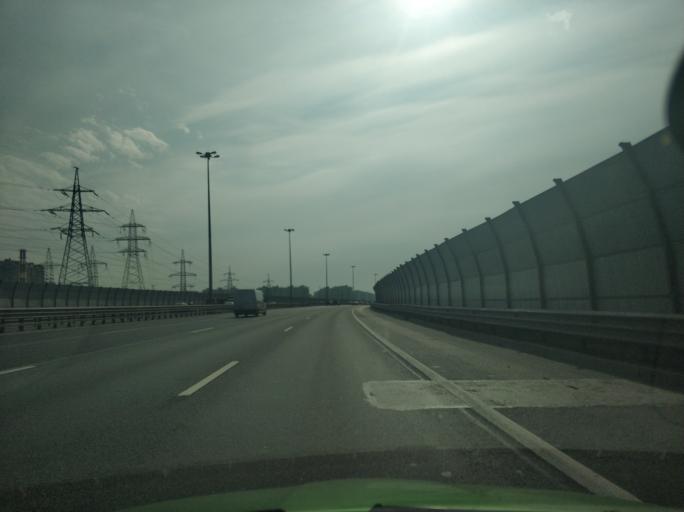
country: RU
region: Leningrad
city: Murino
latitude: 60.0433
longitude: 30.4359
